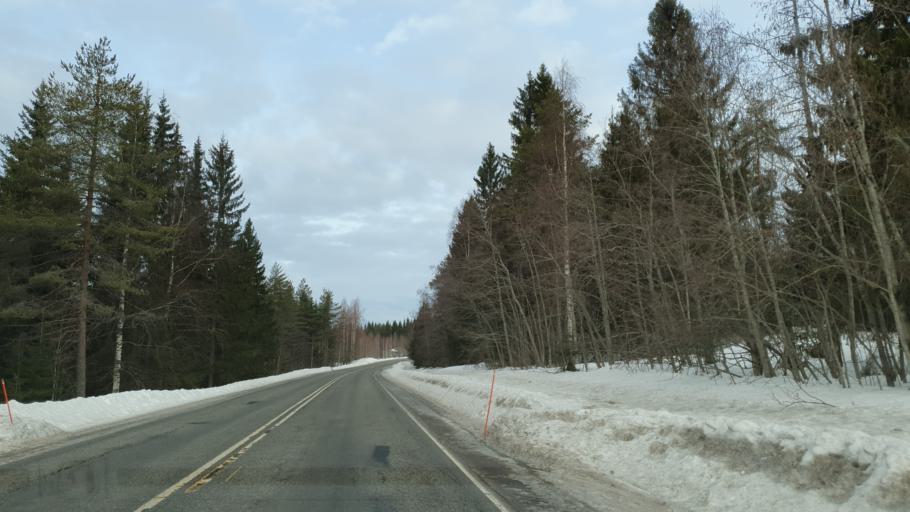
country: FI
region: Kainuu
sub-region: Kajaani
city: Vuokatti
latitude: 64.2498
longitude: 28.0472
